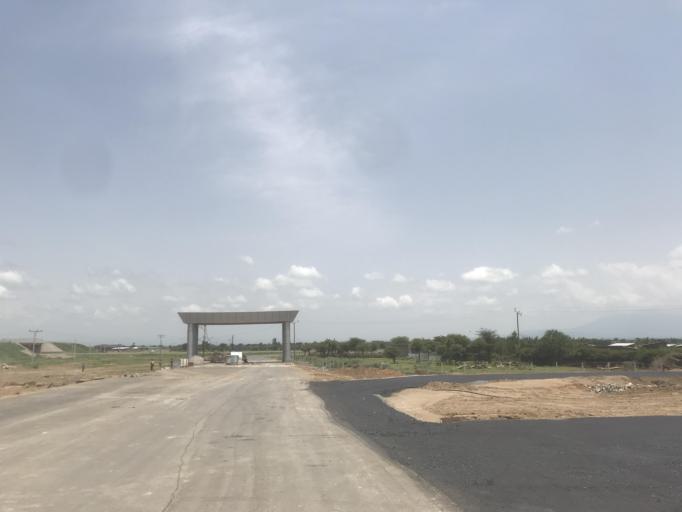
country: ET
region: Oromiya
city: Mojo
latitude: 8.3011
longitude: 38.9399
